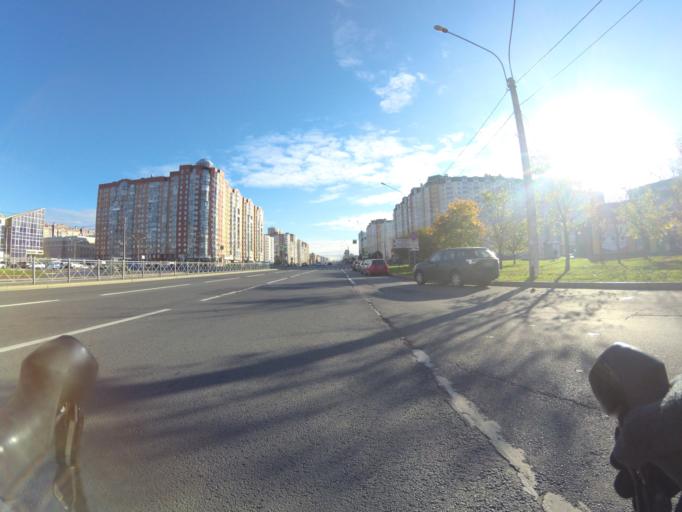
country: RU
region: Leningrad
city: Untolovo
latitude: 60.0070
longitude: 30.2103
